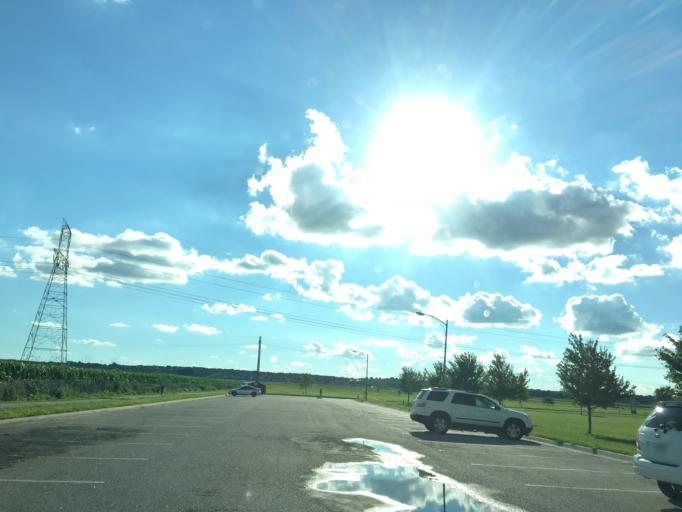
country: US
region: Nebraska
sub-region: Sarpy County
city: La Vista
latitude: 41.1740
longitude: -95.9935
